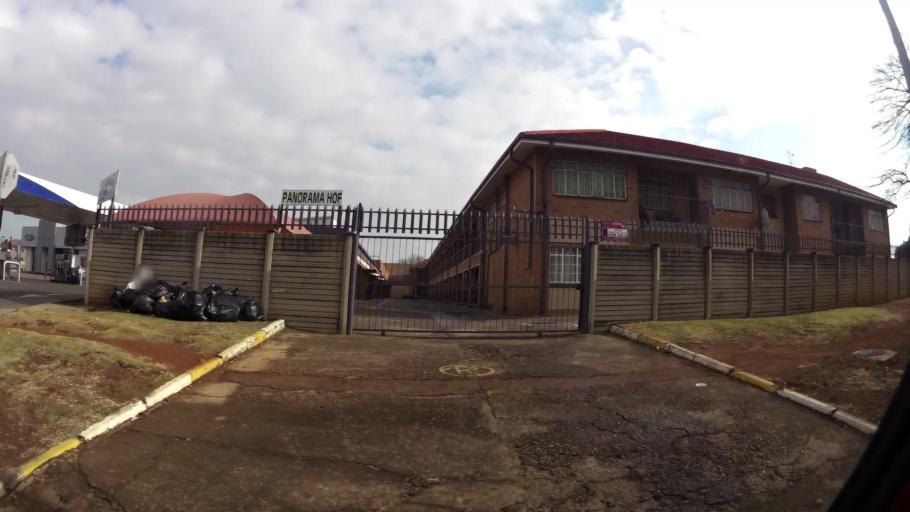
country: ZA
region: Gauteng
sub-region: Sedibeng District Municipality
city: Vanderbijlpark
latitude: -26.6942
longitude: 27.8342
